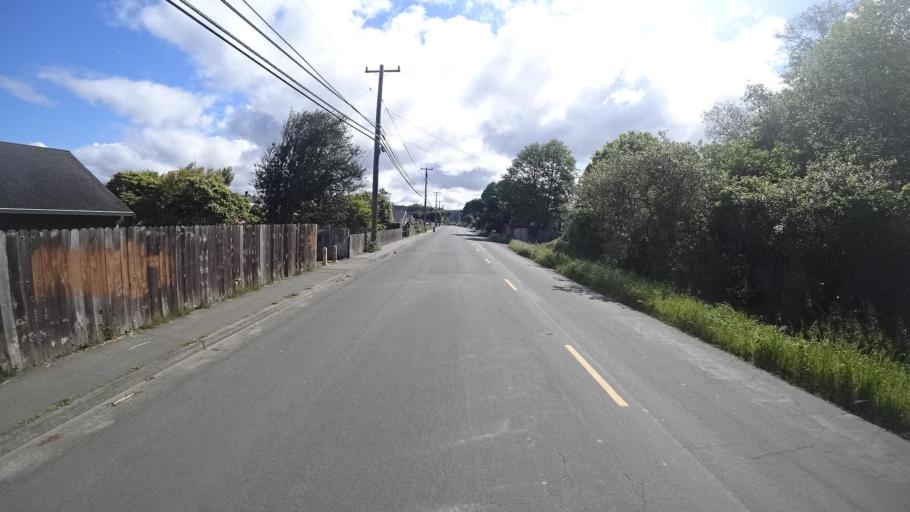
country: US
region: California
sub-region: Humboldt County
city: McKinleyville
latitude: 40.9454
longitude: -124.1059
